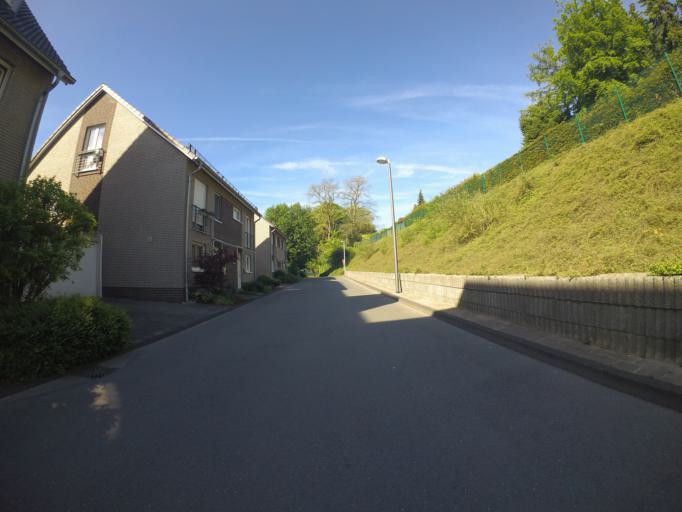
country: DE
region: North Rhine-Westphalia
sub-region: Regierungsbezirk Arnsberg
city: Schwelm
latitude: 51.2728
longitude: 7.2418
